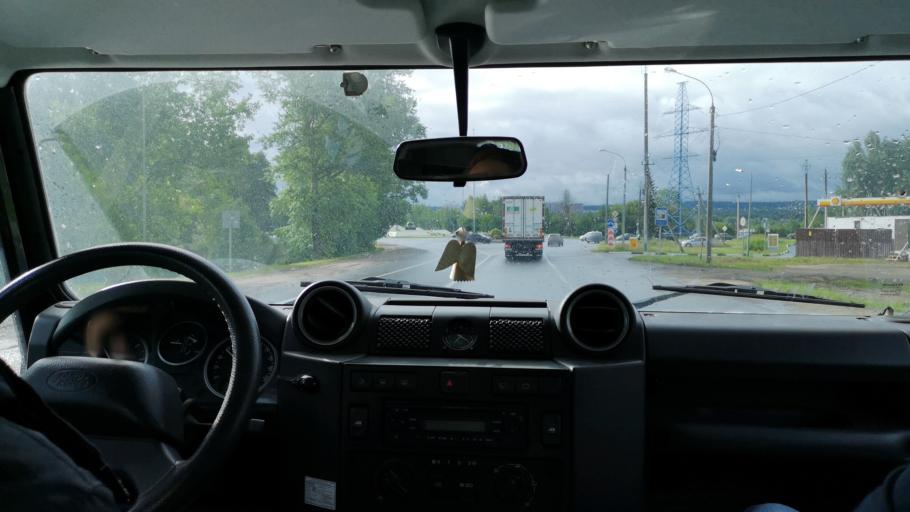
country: RU
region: Moskovskaya
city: Dmitrov
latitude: 56.3589
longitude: 37.4870
